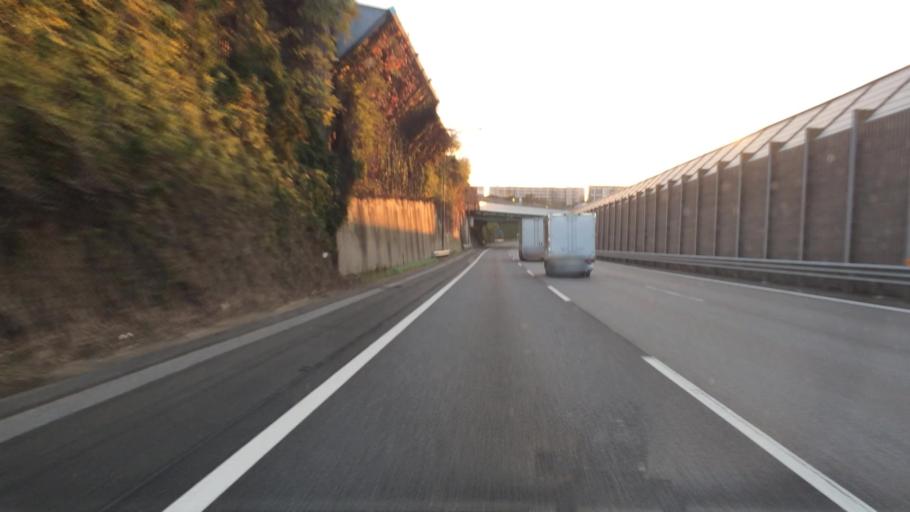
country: JP
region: Chiba
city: Chiba
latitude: 35.6442
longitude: 140.0811
